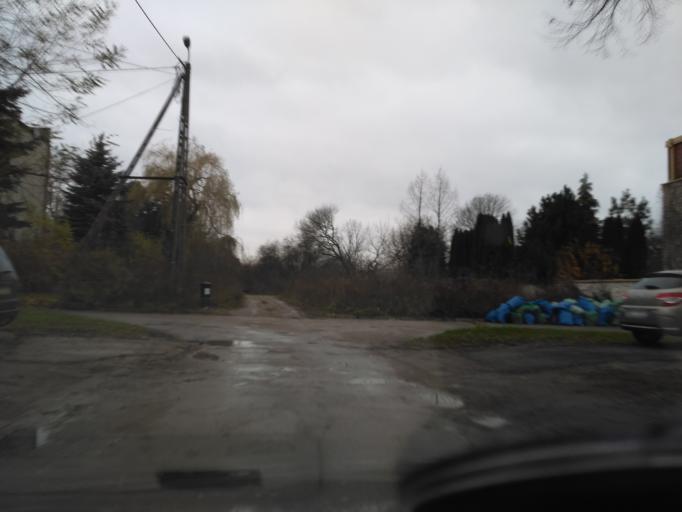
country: PL
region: Lublin Voivodeship
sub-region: Powiat lubelski
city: Lublin
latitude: 51.2656
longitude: 22.5401
